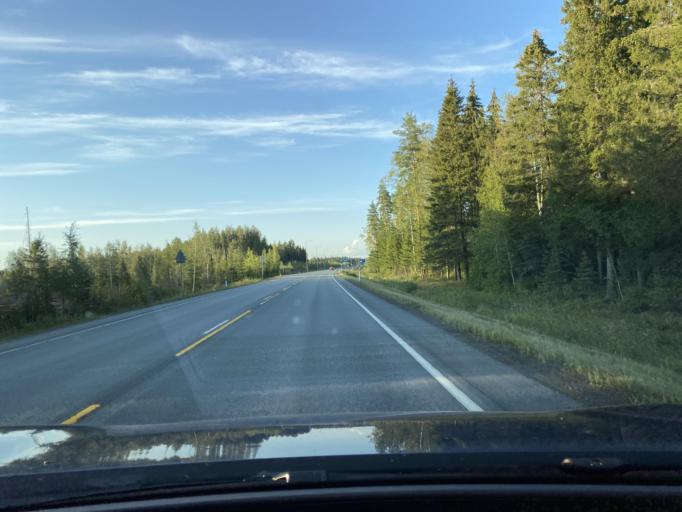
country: FI
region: Southern Ostrobothnia
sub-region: Seinaejoki
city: Seinaejoki
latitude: 62.6828
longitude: 22.7996
